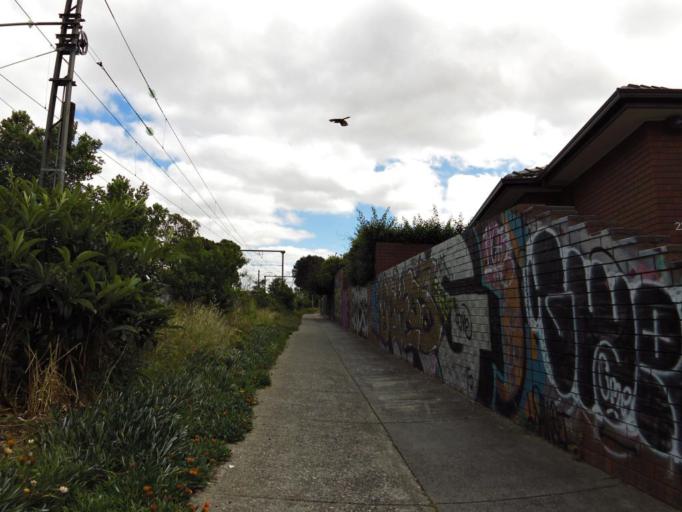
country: AU
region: Victoria
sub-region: Moreland
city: Coburg North
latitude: -37.7359
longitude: 144.9631
